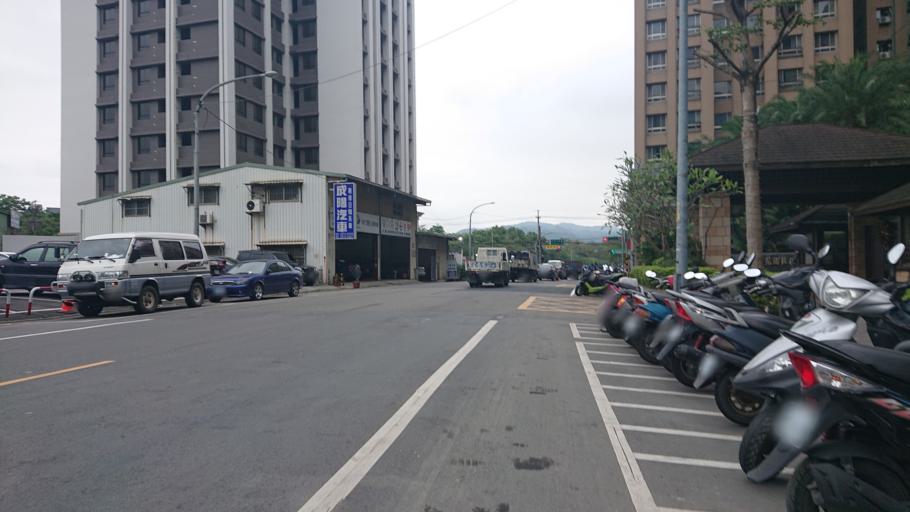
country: TW
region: Taiwan
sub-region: Taoyuan
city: Taoyuan
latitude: 24.9372
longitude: 121.3606
